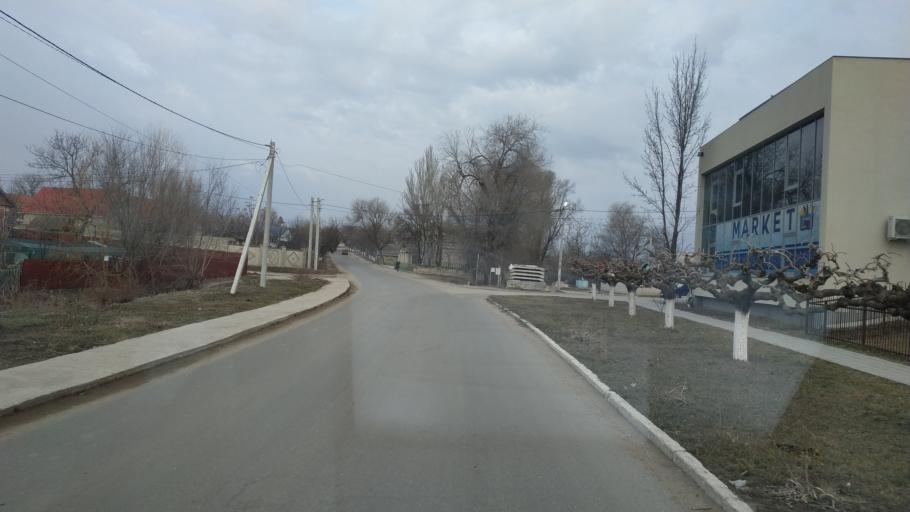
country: MD
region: Chisinau
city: Singera
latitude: 46.9656
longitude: 29.0538
